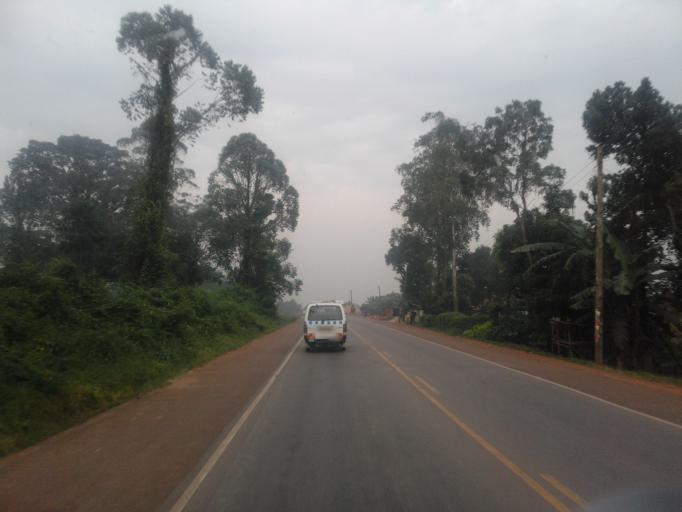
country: UG
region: Central Region
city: Lugazi
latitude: 0.3708
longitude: 32.8798
